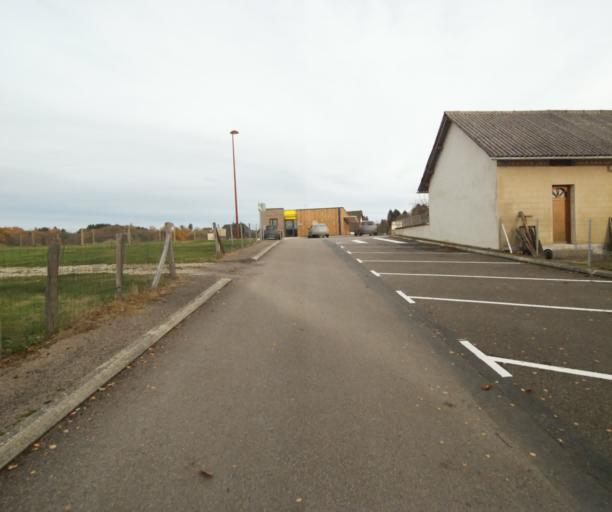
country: FR
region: Limousin
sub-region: Departement de la Correze
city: Sainte-Fortunade
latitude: 45.2109
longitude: 1.7708
